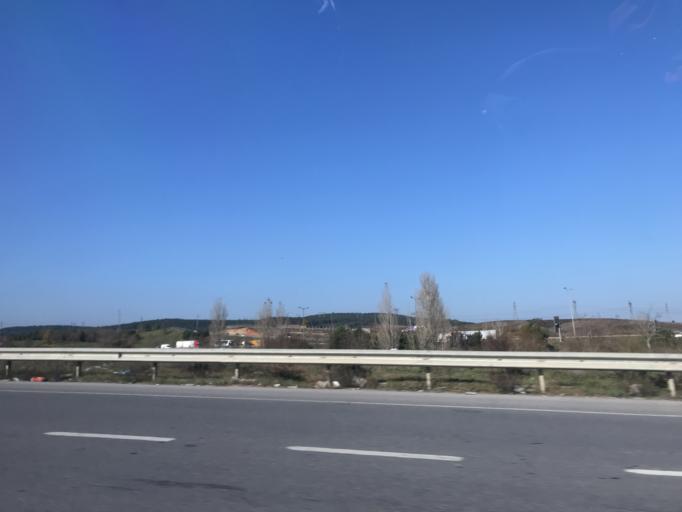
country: TR
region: Istanbul
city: Sultanbeyli
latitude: 40.9328
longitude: 29.3369
